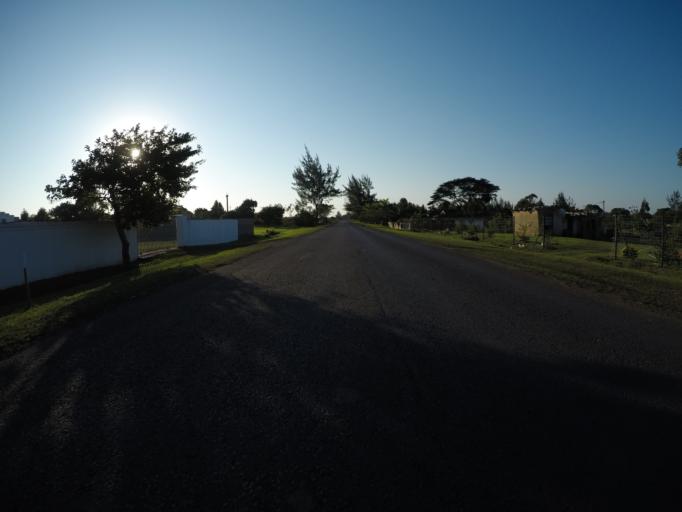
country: ZA
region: KwaZulu-Natal
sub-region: uThungulu District Municipality
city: KwaMbonambi
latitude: -28.6881
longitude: 32.2070
